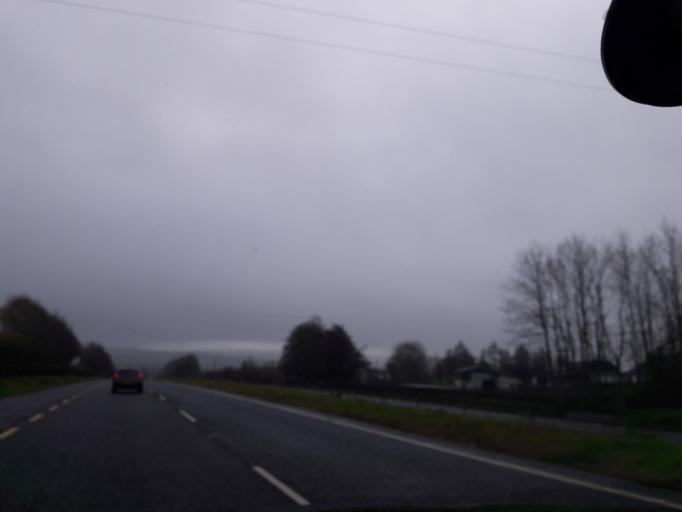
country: IE
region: Ulster
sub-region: County Donegal
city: Letterkenny
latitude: 54.9501
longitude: -7.6541
